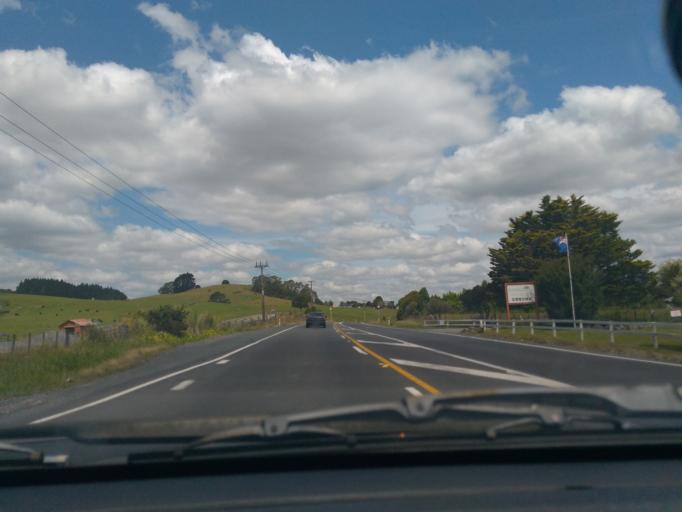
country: NZ
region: Northland
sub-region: Far North District
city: Kerikeri
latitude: -35.3033
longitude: 173.9621
